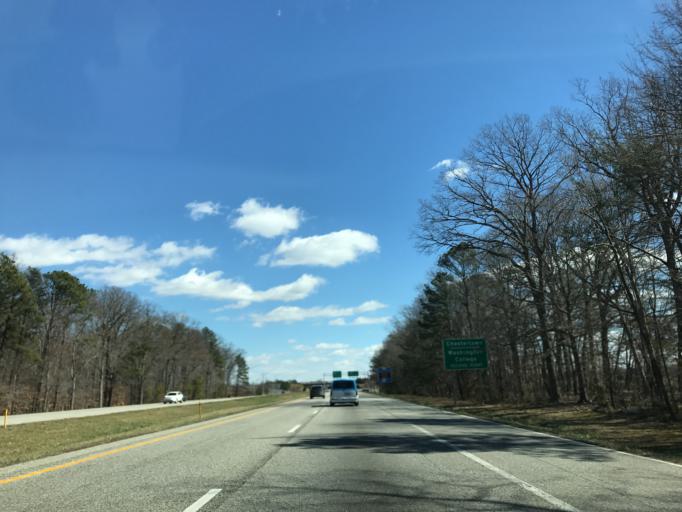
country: US
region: Maryland
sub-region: Queen Anne's County
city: Centreville
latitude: 39.0141
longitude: -76.0838
